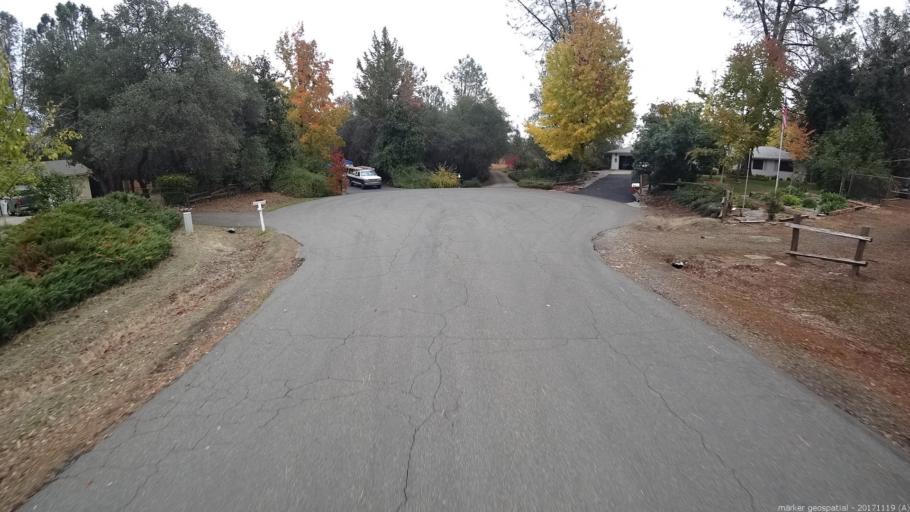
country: US
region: California
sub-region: Shasta County
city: Redding
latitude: 40.4925
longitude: -122.4131
